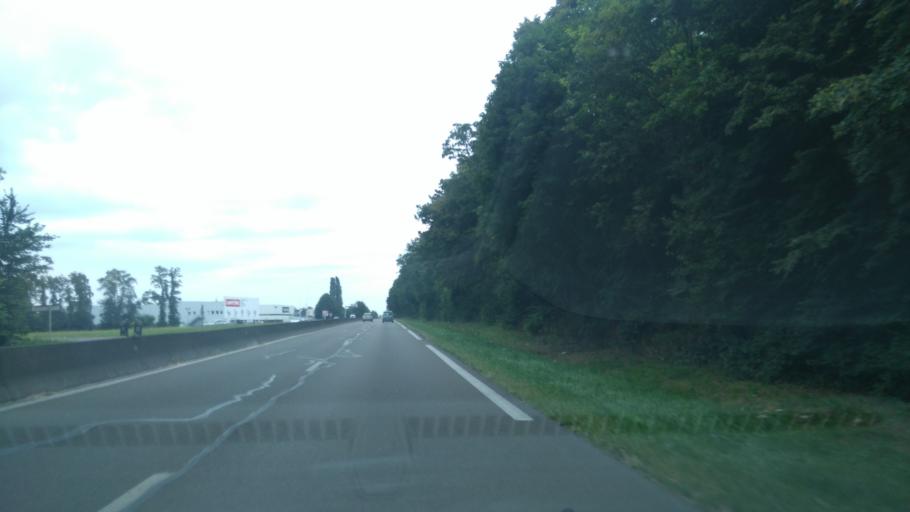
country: FR
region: Picardie
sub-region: Departement de l'Oise
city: Saint-Maximin
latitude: 49.2276
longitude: 2.4694
